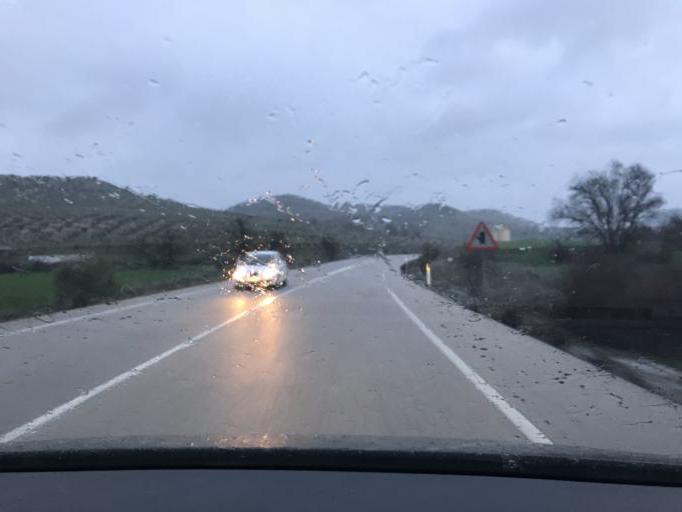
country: ES
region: Andalusia
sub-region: Provincia de Granada
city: Campotejar
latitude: 37.4523
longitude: -3.6369
